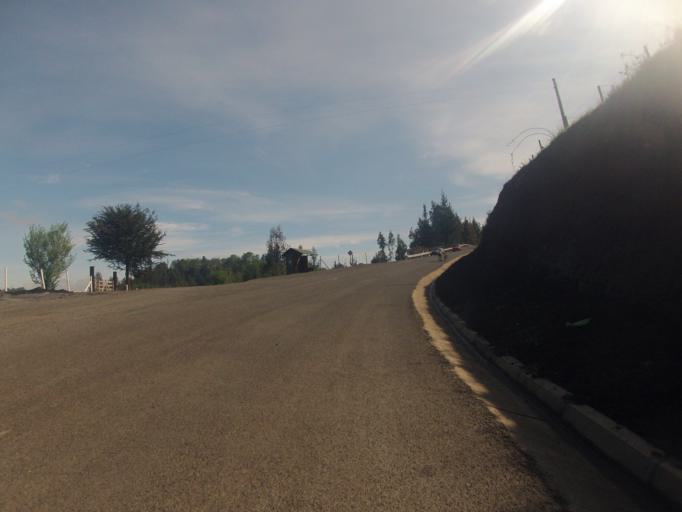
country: CL
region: Araucania
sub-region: Provincia de Cautin
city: Temuco
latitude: -38.7040
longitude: -72.5942
